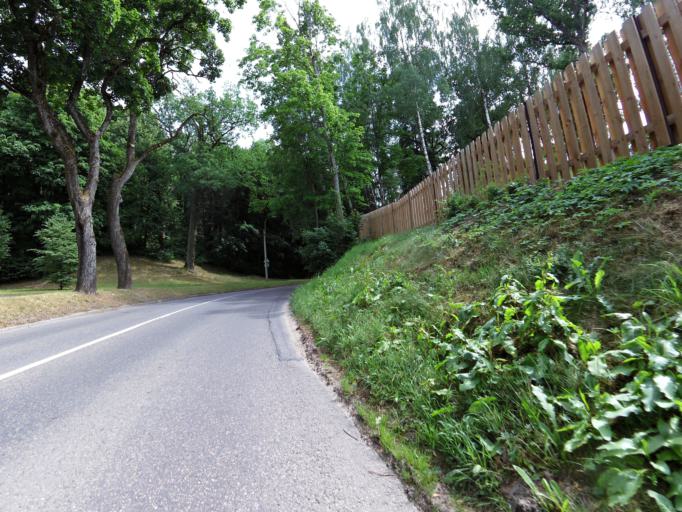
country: LT
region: Vilnius County
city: Rasos
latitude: 54.6740
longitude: 25.3227
